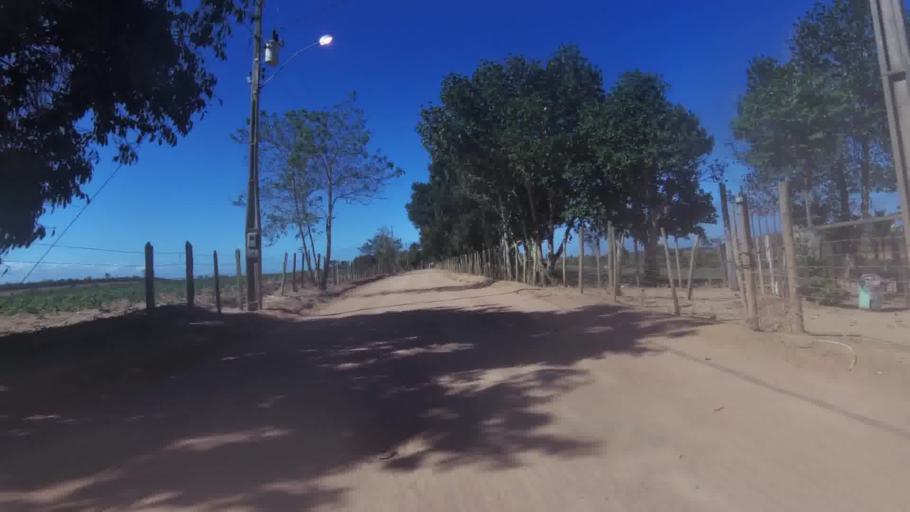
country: BR
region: Espirito Santo
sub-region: Marataizes
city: Marataizes
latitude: -21.1351
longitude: -40.9911
